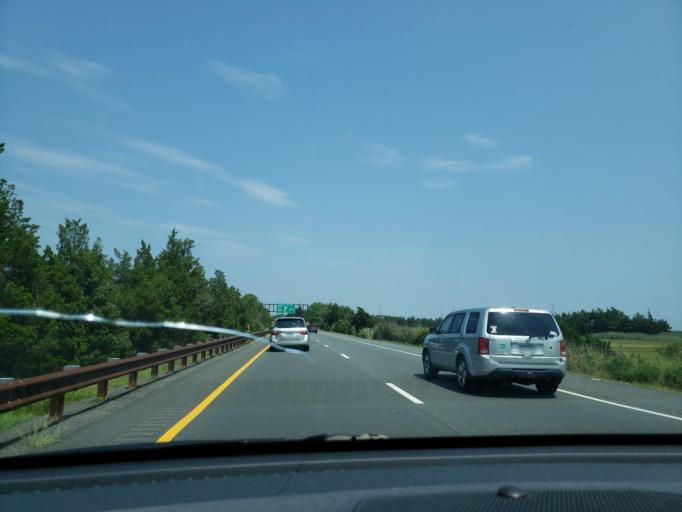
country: US
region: New Jersey
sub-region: Cape May County
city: Sea Isle City
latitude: 39.1682
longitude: -74.7331
